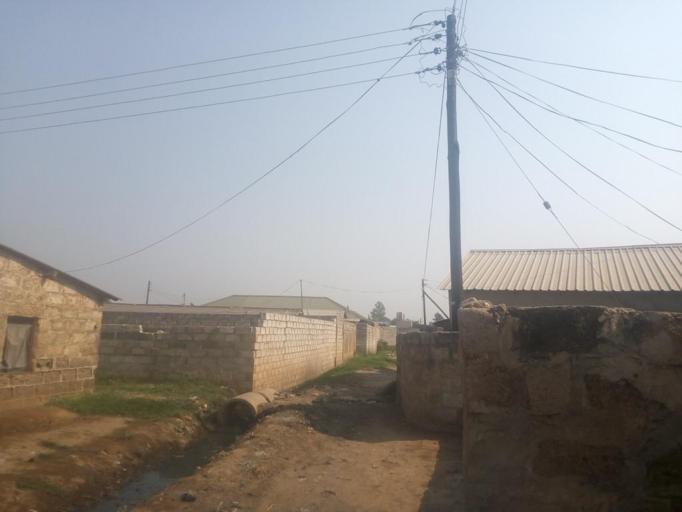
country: ZM
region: Lusaka
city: Lusaka
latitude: -15.4065
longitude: 28.3613
